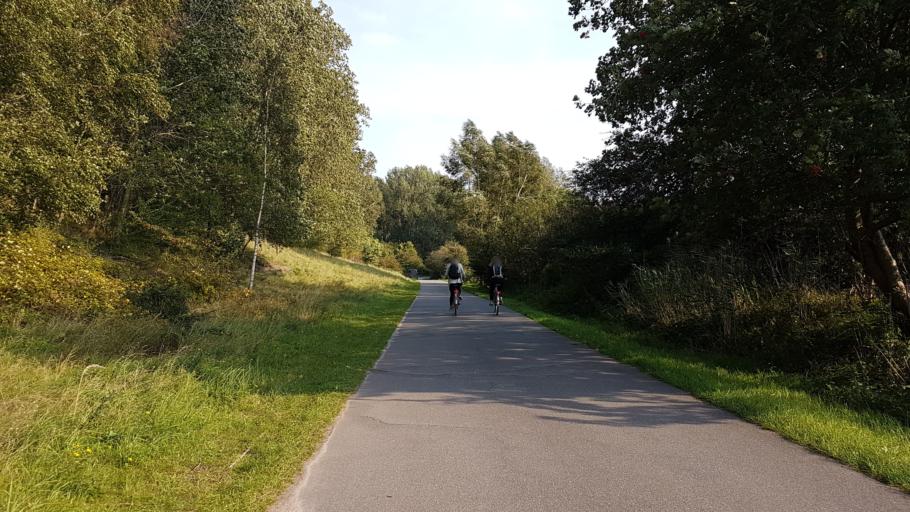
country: DE
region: Mecklenburg-Vorpommern
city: Glowe
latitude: 54.5637
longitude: 13.4771
